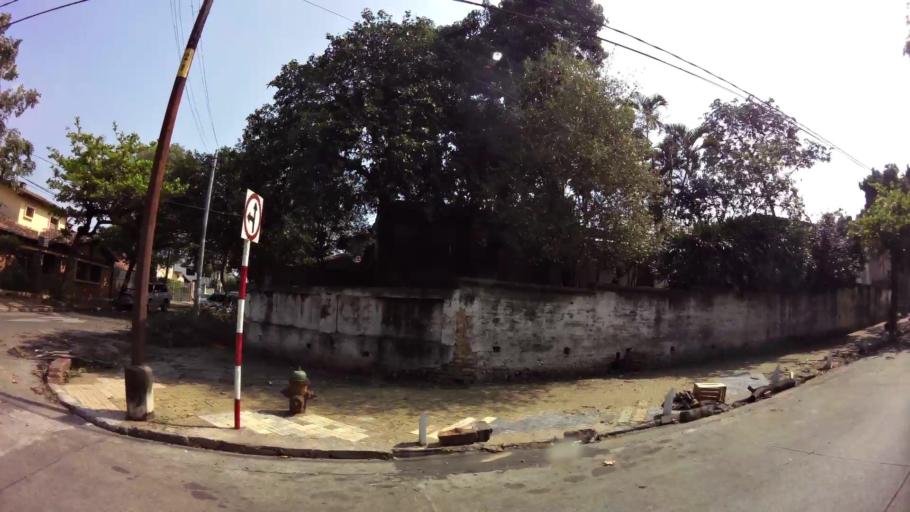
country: PY
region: Presidente Hayes
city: Nanawa
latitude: -25.2889
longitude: -57.6621
